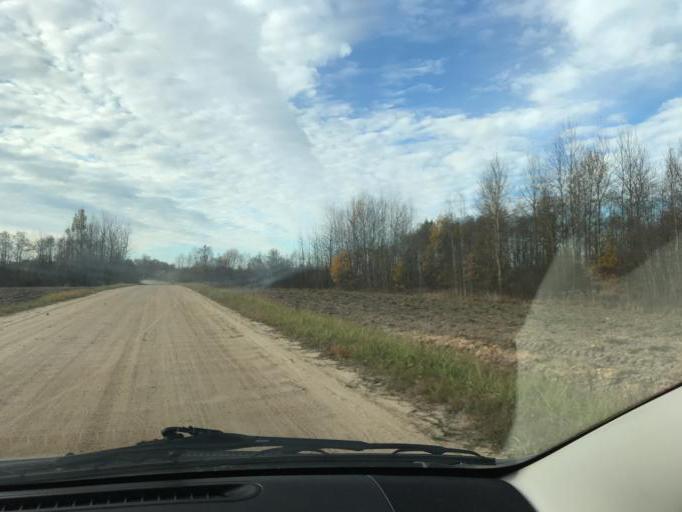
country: BY
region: Vitebsk
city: Haradok
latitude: 55.4576
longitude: 30.0436
